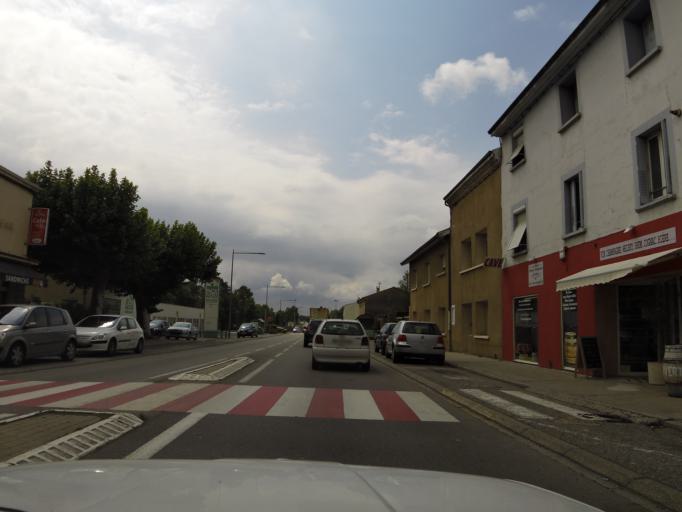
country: FR
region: Rhone-Alpes
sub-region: Departement de la Drome
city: La Roche-de-Glun
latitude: 45.0035
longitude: 4.8714
